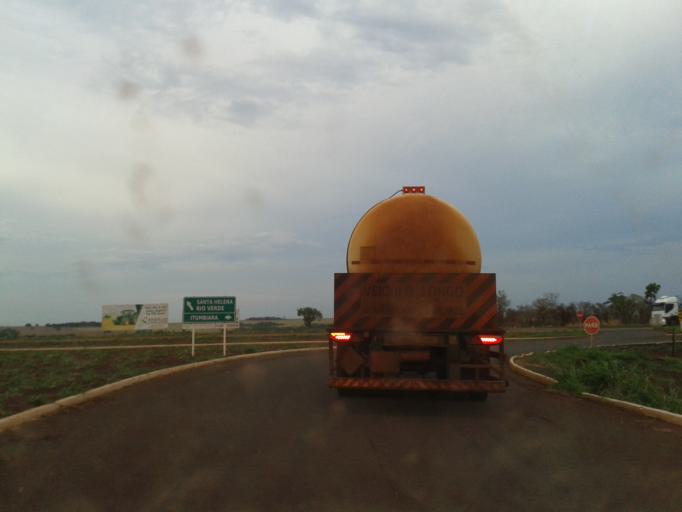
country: BR
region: Goias
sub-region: Santa Helena De Goias
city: Santa Helena de Goias
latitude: -17.9597
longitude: -50.4968
